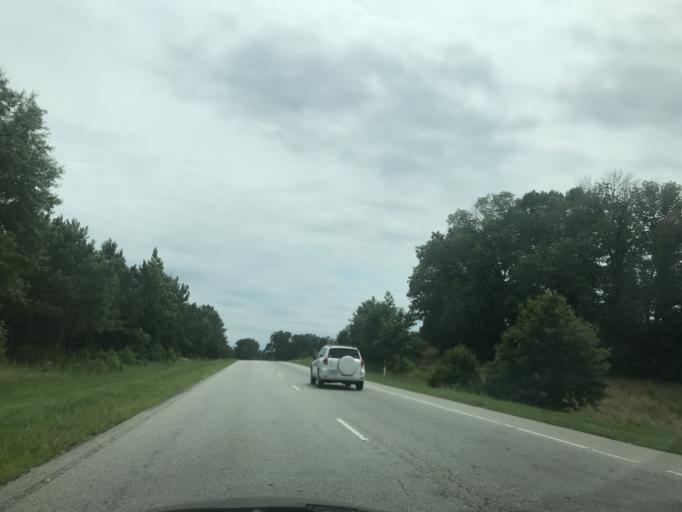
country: US
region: North Carolina
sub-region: Franklin County
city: Franklinton
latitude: 36.1644
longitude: -78.4519
